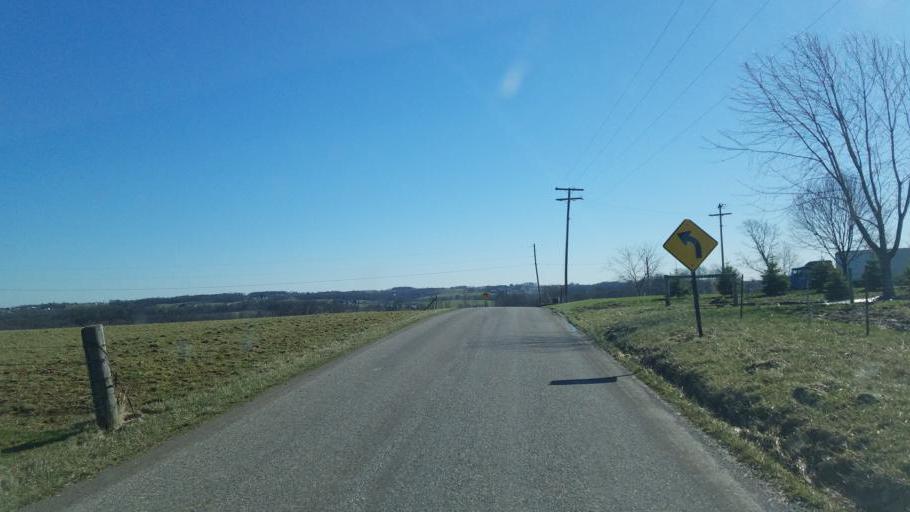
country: US
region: Ohio
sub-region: Wayne County
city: Apple Creek
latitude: 40.6531
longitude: -81.8329
